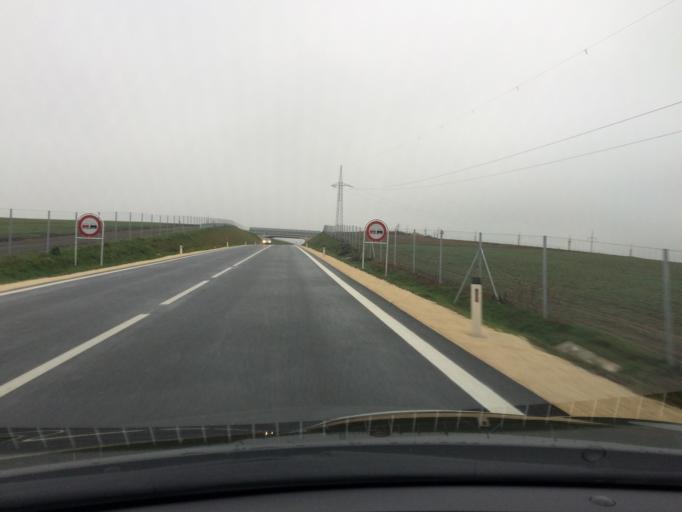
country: AT
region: Lower Austria
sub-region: Politischer Bezirk Mistelbach
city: Mistelbach
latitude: 48.5475
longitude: 16.5701
